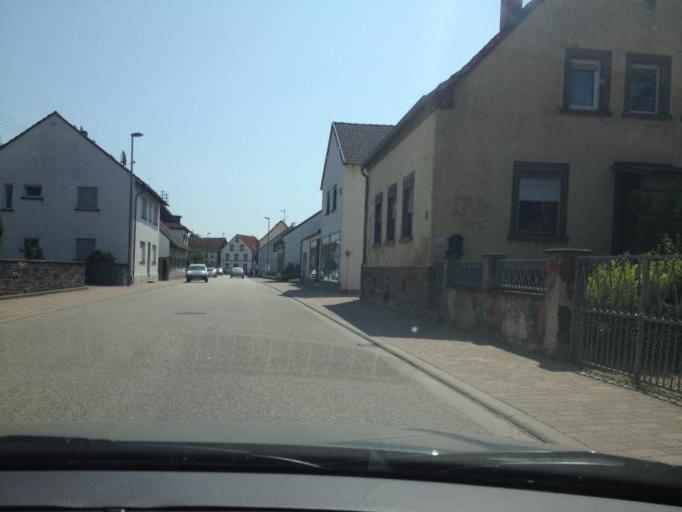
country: DE
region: Rheinland-Pfalz
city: Bruchmuhlbach-Miesau
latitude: 49.4080
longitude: 7.4291
